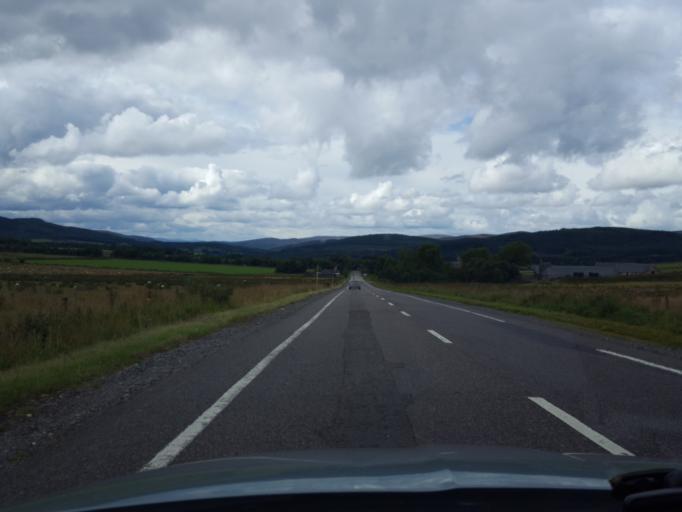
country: GB
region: Scotland
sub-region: Moray
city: Rothes
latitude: 57.4317
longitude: -3.3299
